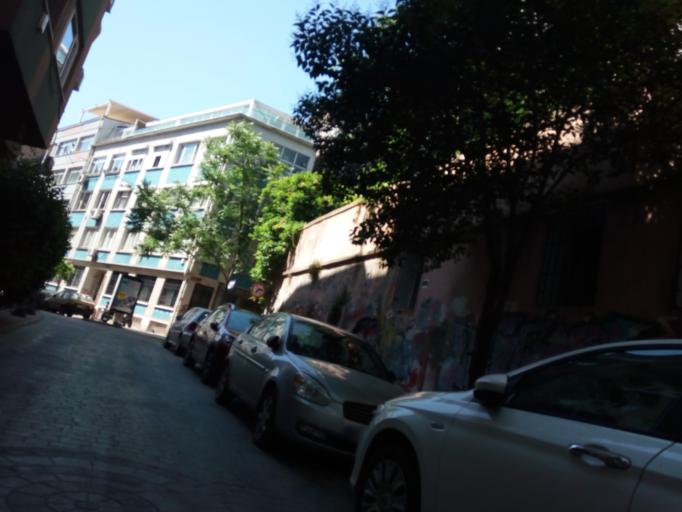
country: TR
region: Istanbul
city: Eminoenue
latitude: 41.0328
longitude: 28.9851
